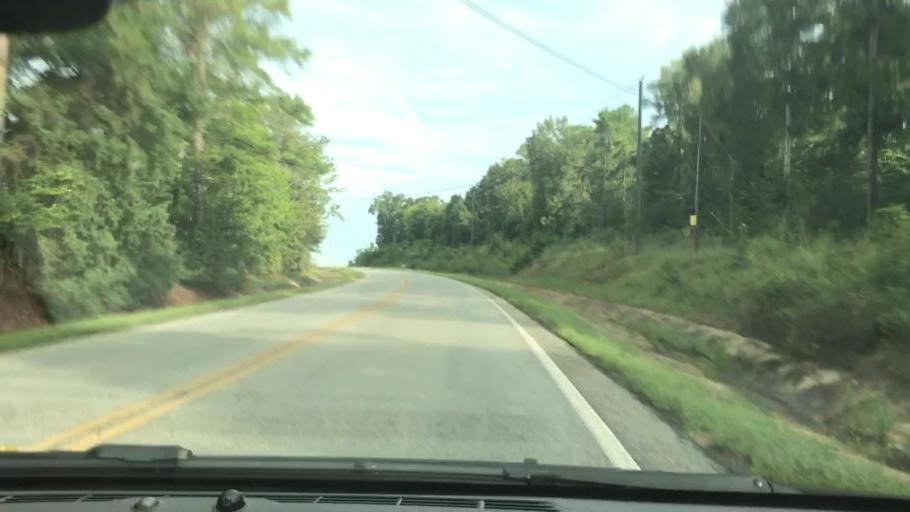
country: US
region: Georgia
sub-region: Quitman County
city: Georgetown
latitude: 31.7532
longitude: -85.0572
